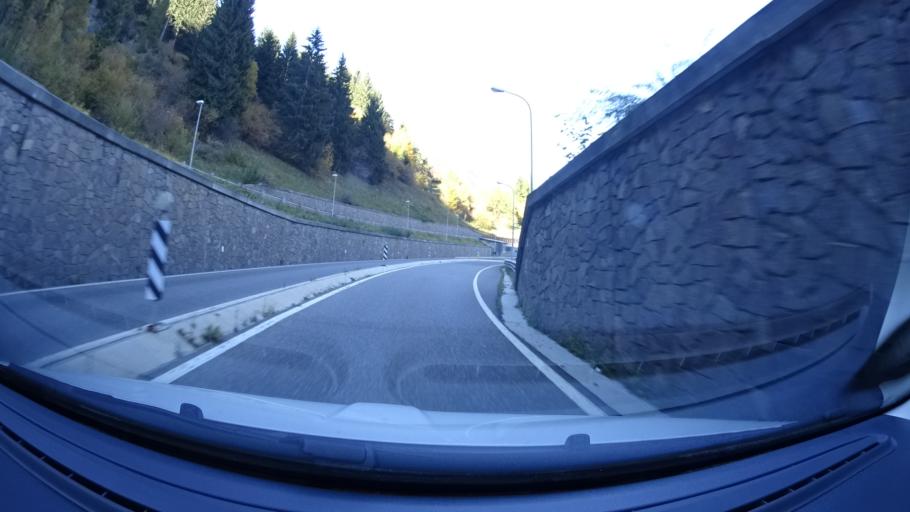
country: IT
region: Trentino-Alto Adige
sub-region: Provincia di Trento
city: Predazzo
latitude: 46.3188
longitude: 11.5948
